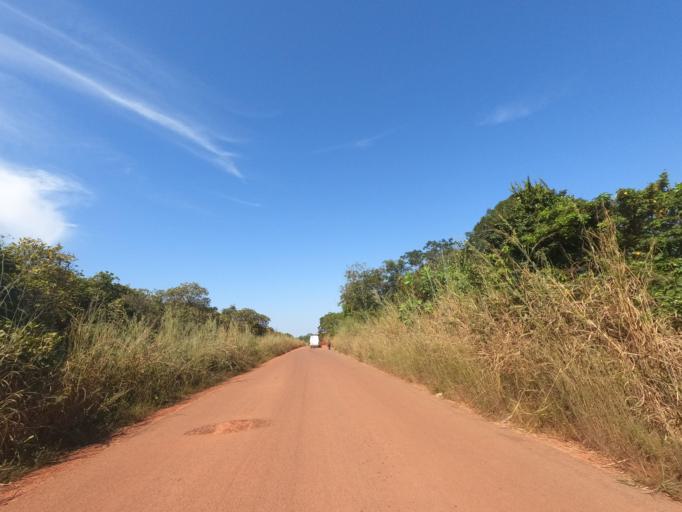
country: SN
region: Ziguinchor
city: Adeane
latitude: 12.3939
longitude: -15.8859
